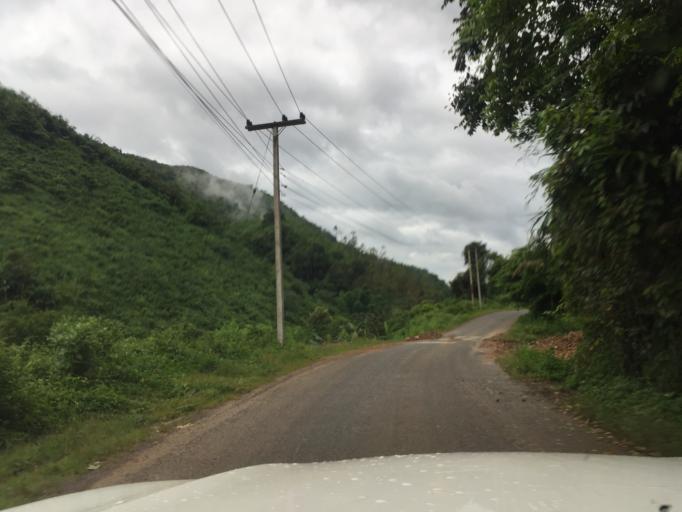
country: LA
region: Oudomxai
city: Muang La
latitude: 20.9933
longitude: 102.2300
